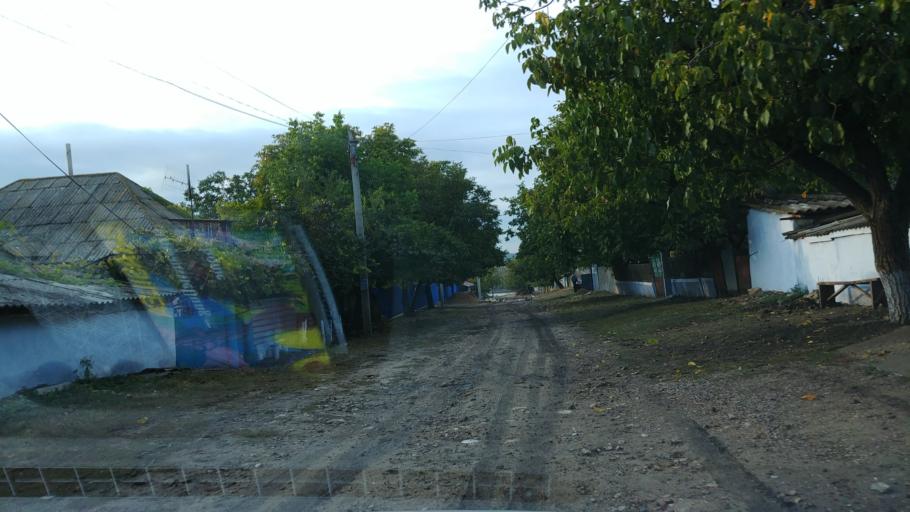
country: MD
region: Rezina
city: Saharna
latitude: 47.6780
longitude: 28.9593
